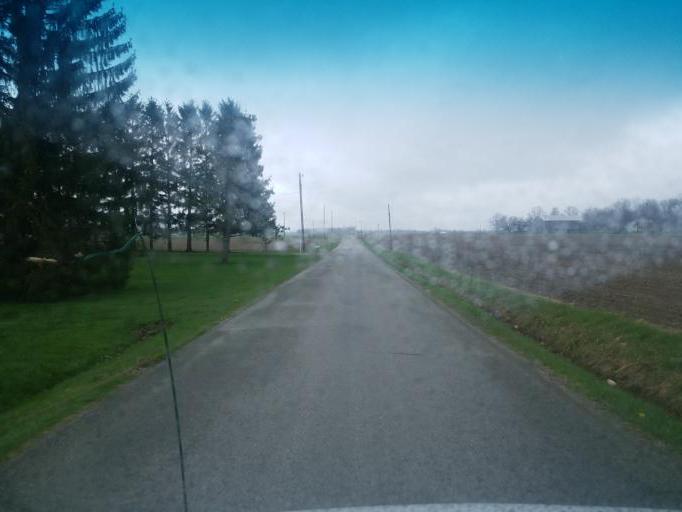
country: US
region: Ohio
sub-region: Richland County
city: Shelby
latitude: 40.9111
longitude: -82.6186
